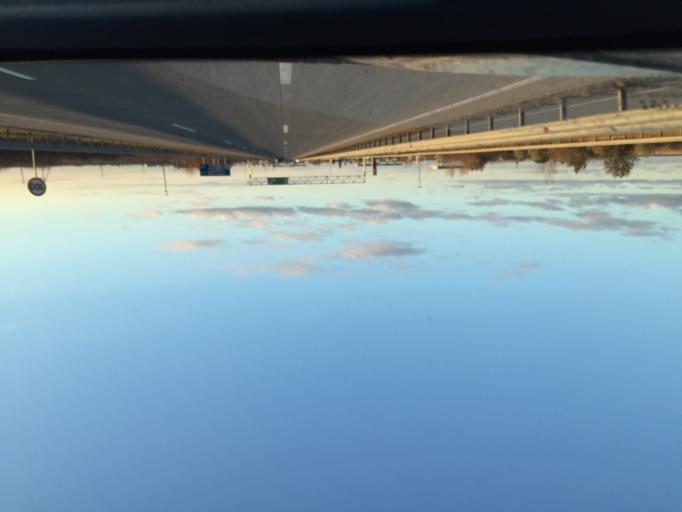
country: KZ
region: Astana Qalasy
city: Astana
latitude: 51.2725
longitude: 71.3667
